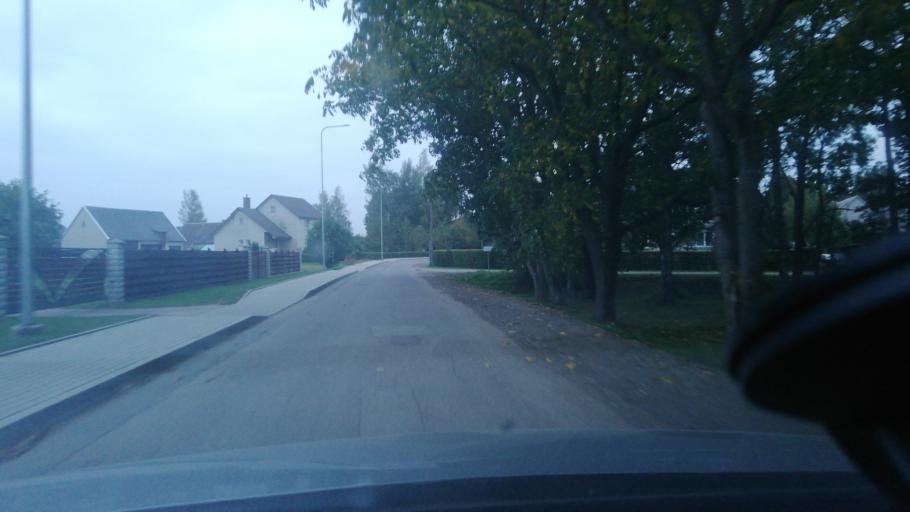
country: LT
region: Klaipedos apskritis
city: Kretinga
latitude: 55.9385
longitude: 21.1832
